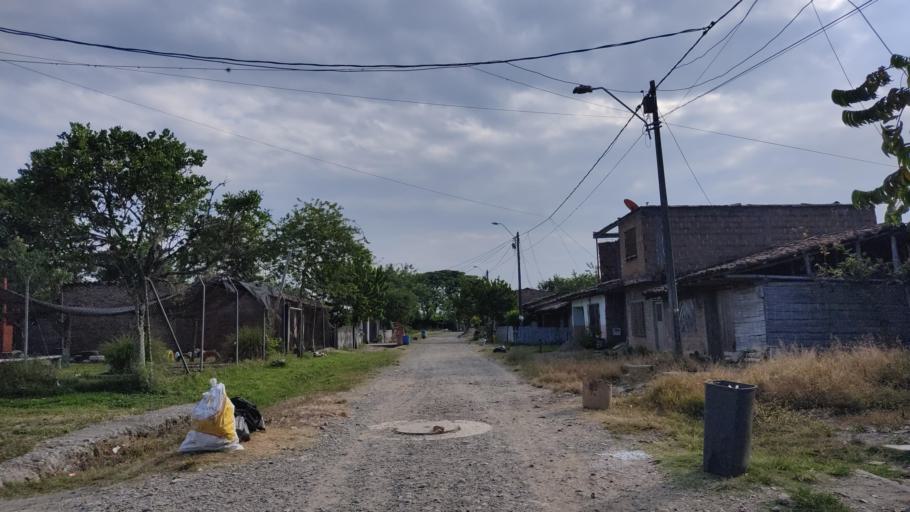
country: CO
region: Valle del Cauca
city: Jamundi
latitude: 3.1295
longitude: -76.5562
